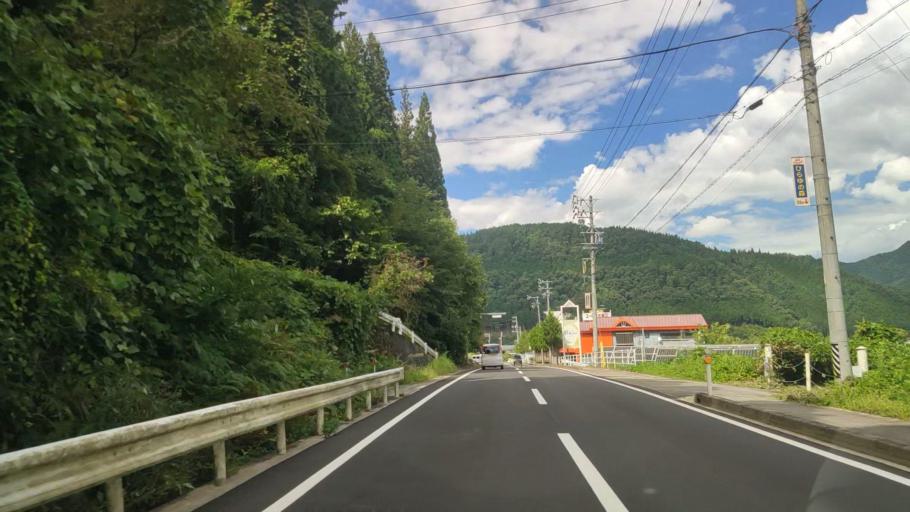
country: JP
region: Gifu
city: Takayama
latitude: 36.1827
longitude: 137.2574
